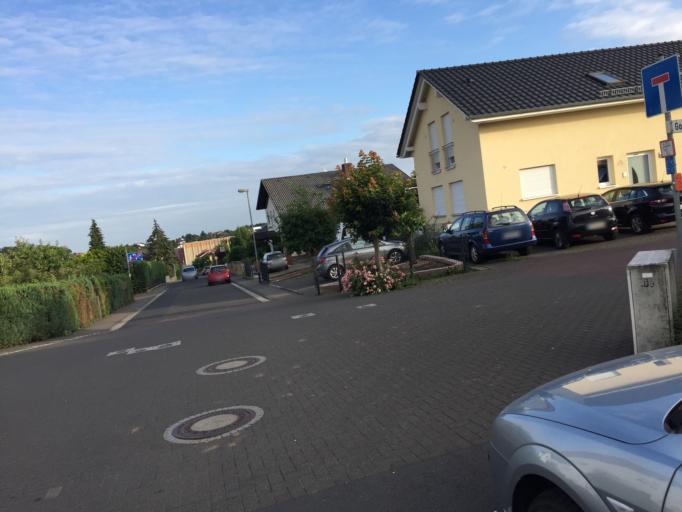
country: DE
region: Hesse
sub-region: Regierungsbezirk Giessen
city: Reiskirchen
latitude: 50.6019
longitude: 8.8248
